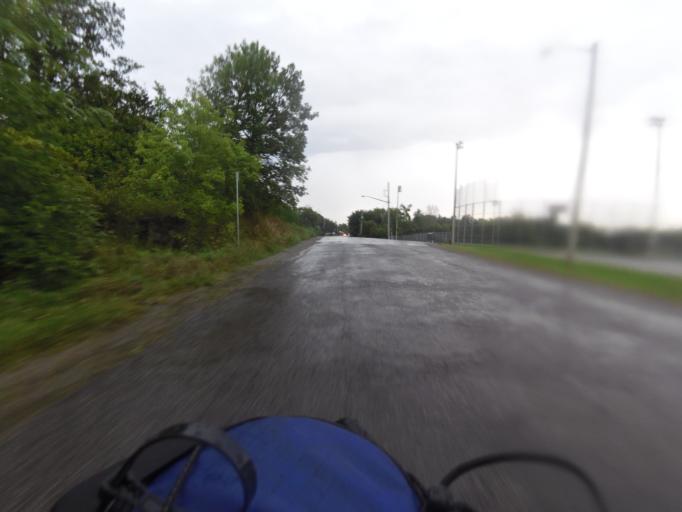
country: CA
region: Ontario
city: Ottawa
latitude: 45.2385
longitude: -75.4772
